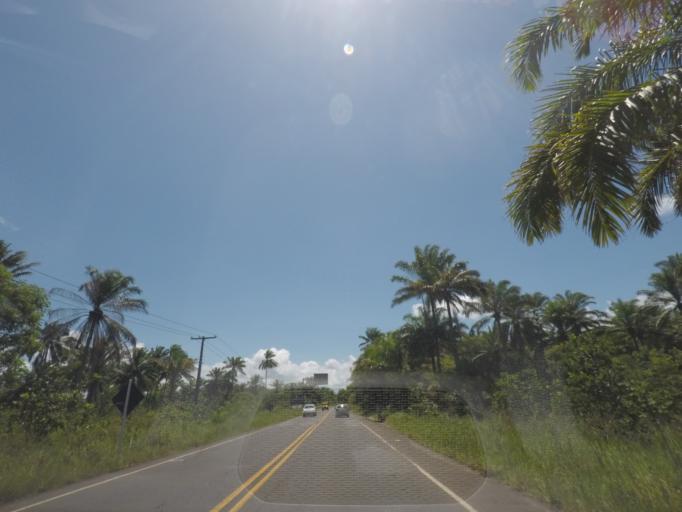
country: BR
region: Bahia
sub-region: Valenca
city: Valenca
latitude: -13.3253
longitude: -39.0422
